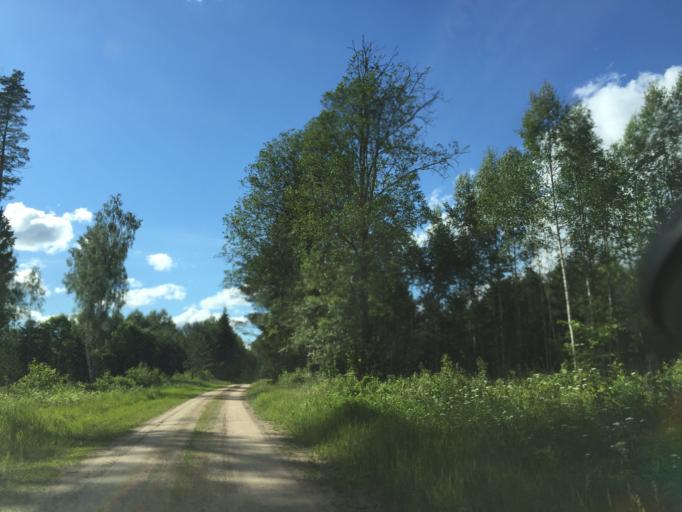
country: LV
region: Vecumnieki
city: Vecumnieki
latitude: 56.4320
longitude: 24.6013
